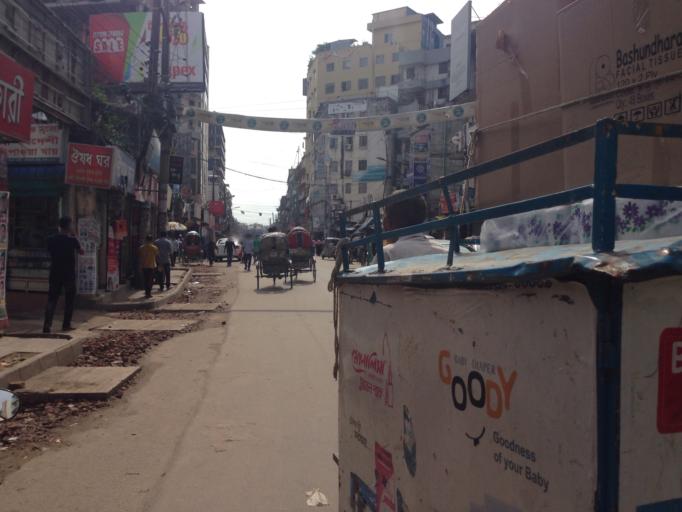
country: BD
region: Dhaka
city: Azimpur
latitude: 23.7368
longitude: 90.3865
